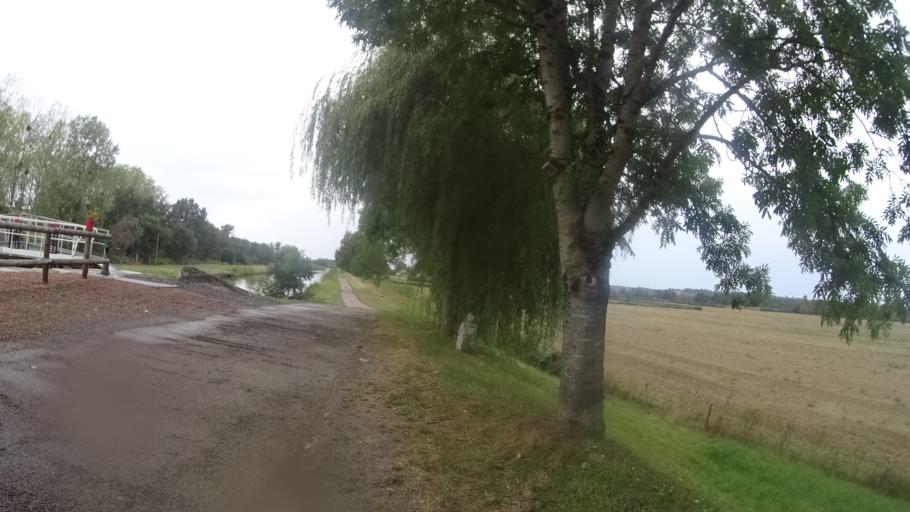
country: FR
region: Bourgogne
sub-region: Departement de la Nievre
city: Saint-Leger-des-Vignes
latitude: 46.8147
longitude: 3.3653
